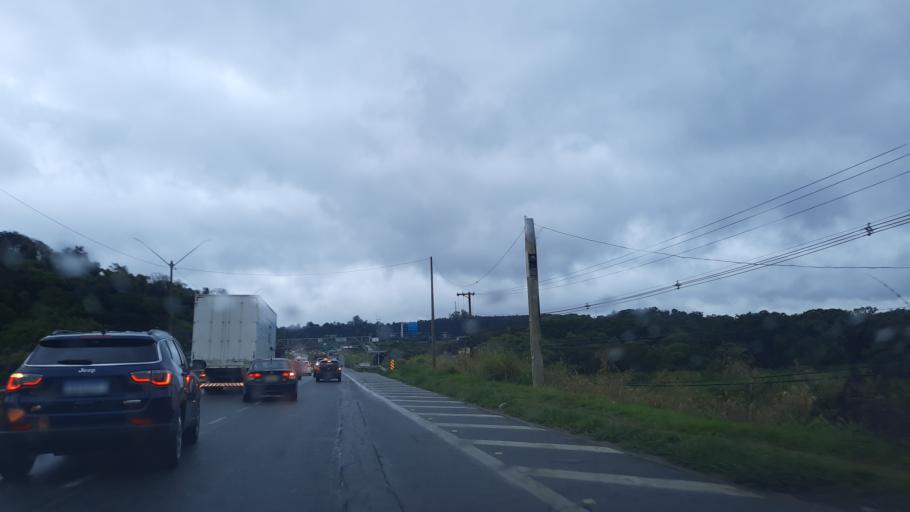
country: BR
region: Sao Paulo
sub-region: Atibaia
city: Atibaia
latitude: -23.1093
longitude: -46.5701
